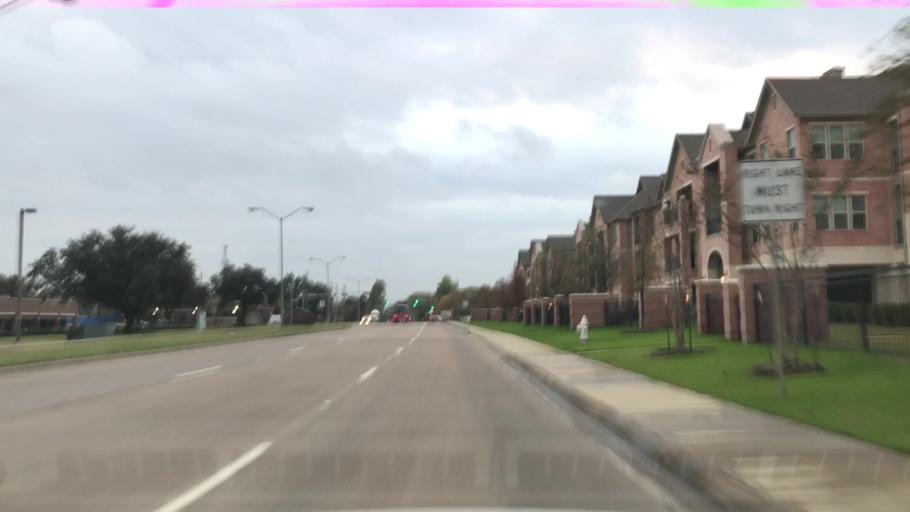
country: US
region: Texas
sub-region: Dallas County
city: Farmers Branch
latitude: 32.8979
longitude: -96.9187
